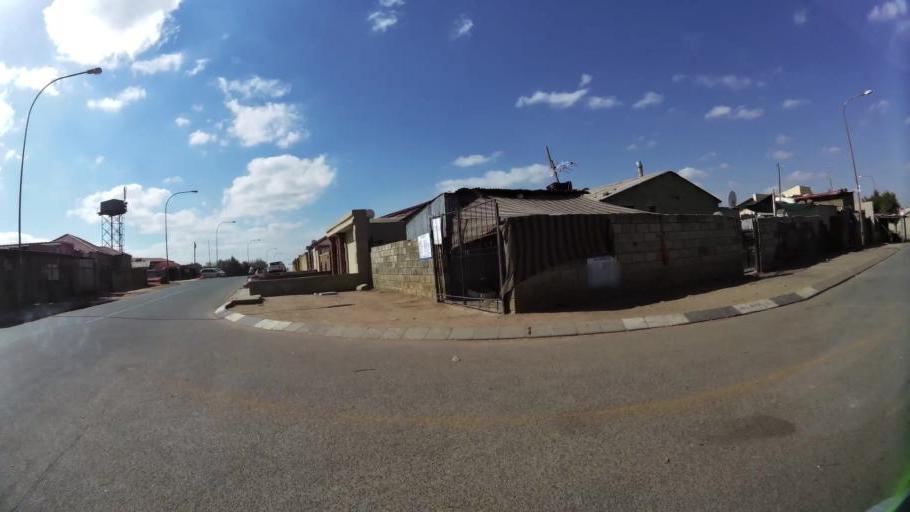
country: ZA
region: Gauteng
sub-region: City of Johannesburg Metropolitan Municipality
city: Soweto
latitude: -26.2307
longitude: 27.8978
